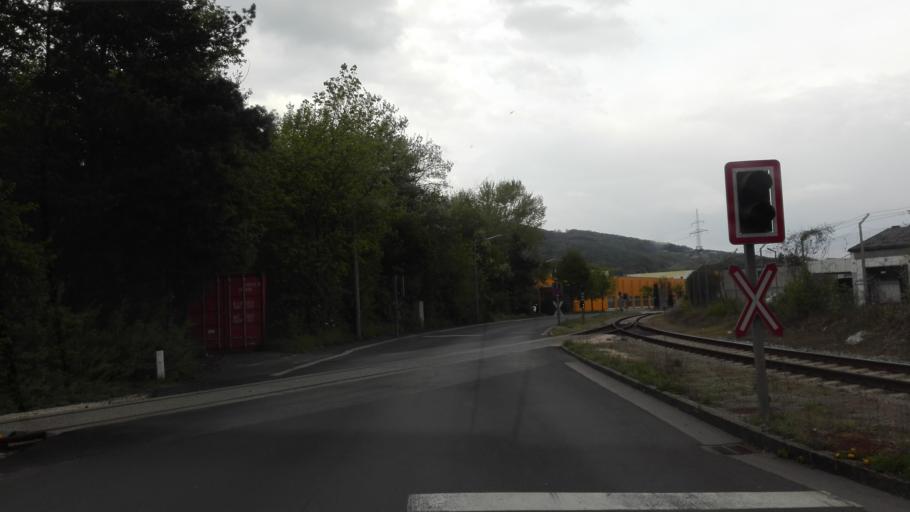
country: AT
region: Upper Austria
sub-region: Linz Stadt
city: Linz
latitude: 48.3105
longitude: 14.3261
